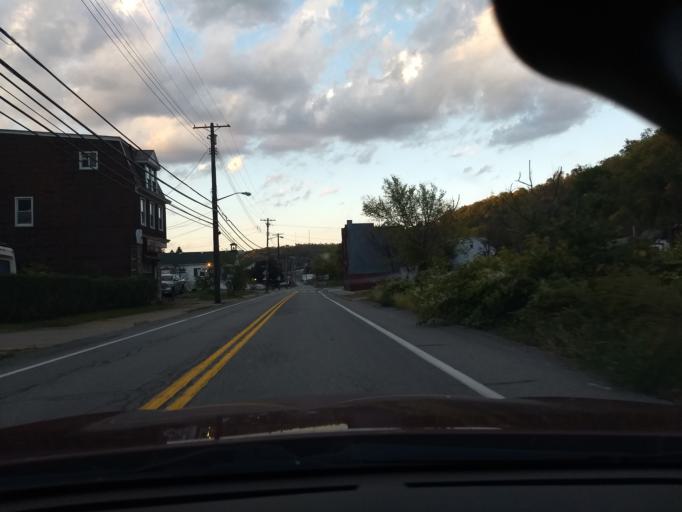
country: US
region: Pennsylvania
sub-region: Allegheny County
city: West Homestead
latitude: 40.3859
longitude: -79.9326
